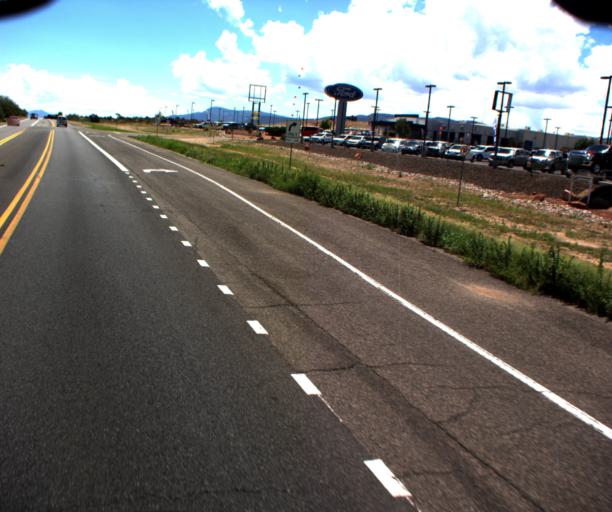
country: US
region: Arizona
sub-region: Yavapai County
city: Cornville
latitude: 34.6523
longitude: -111.9582
